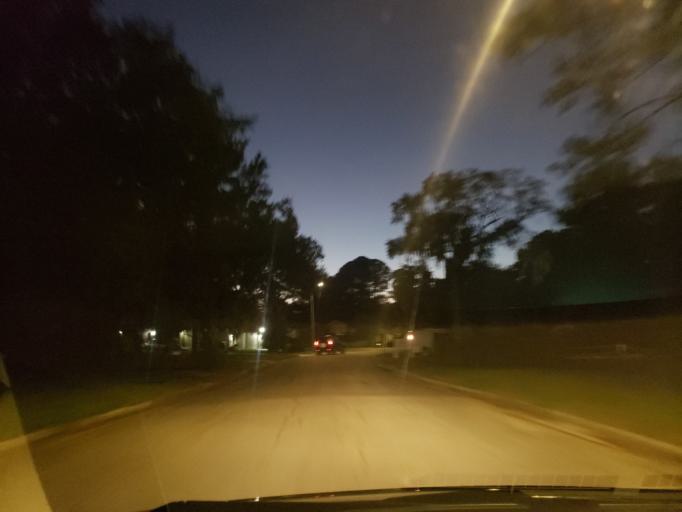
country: US
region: Georgia
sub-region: Chatham County
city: Isle of Hope
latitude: 31.9859
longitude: -81.0604
